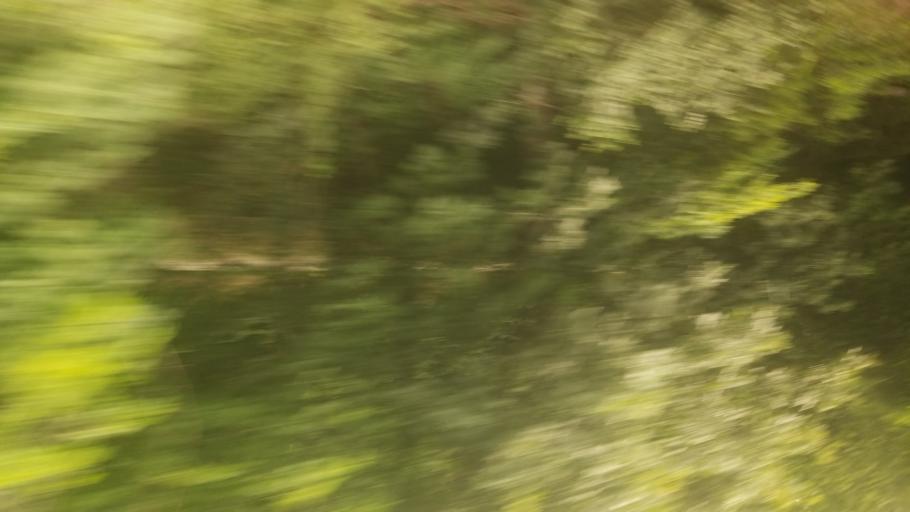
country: US
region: Kansas
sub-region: Douglas County
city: Lawrence
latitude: 39.0319
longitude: -95.3479
